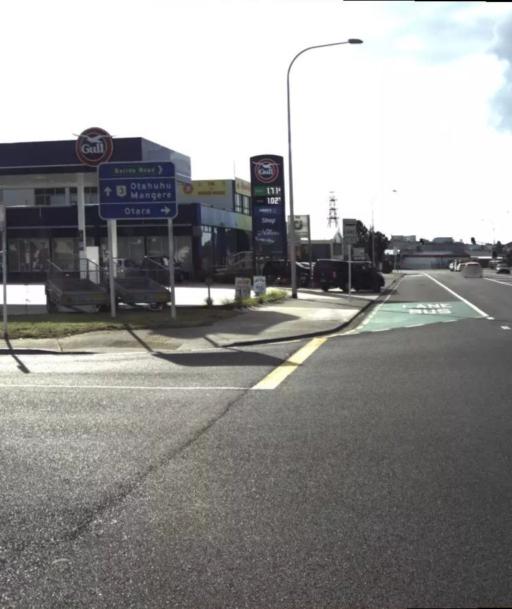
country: NZ
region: Auckland
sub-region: Auckland
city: Wiri
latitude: -36.9590
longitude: 174.8532
